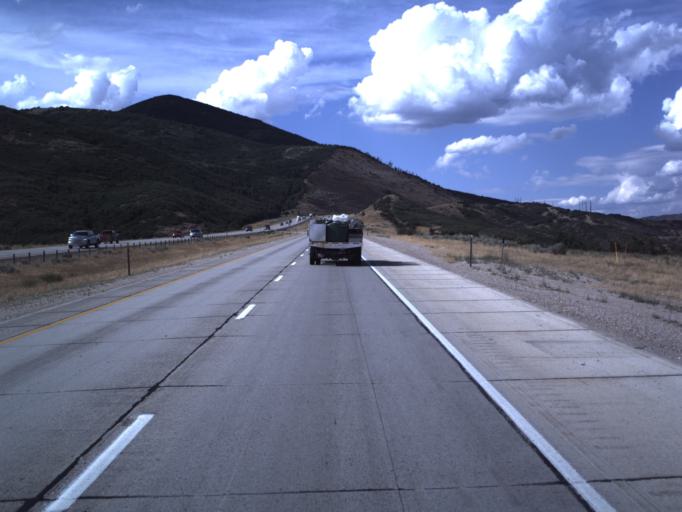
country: US
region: Utah
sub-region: Wasatch County
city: Heber
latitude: 40.5827
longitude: -111.4363
